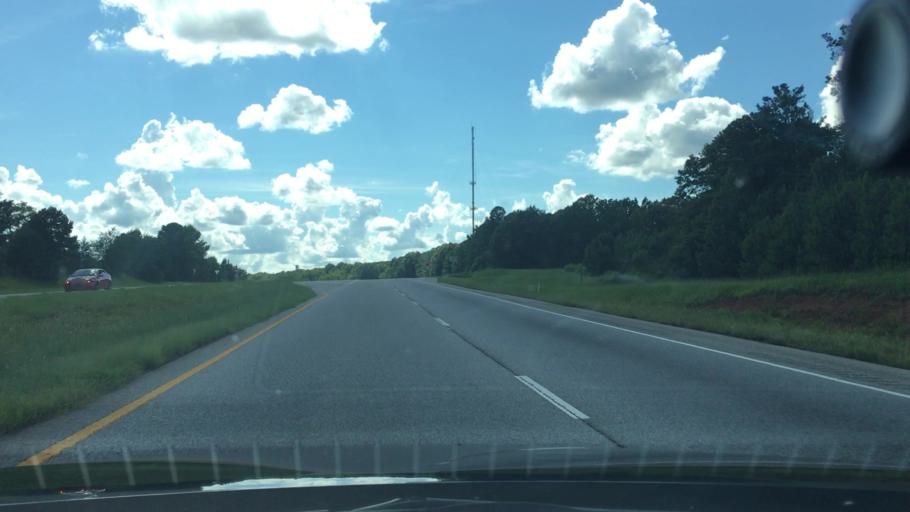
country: US
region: Georgia
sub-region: Spalding County
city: East Griffin
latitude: 33.2382
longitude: -84.2034
